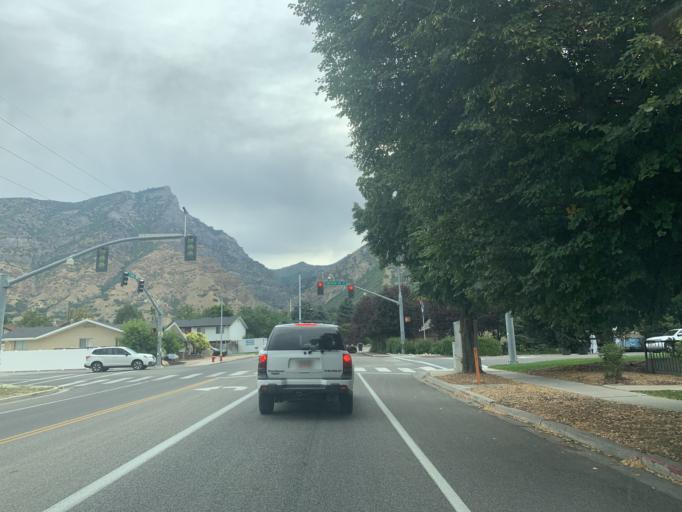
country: US
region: Utah
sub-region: Utah County
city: Provo
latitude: 40.2631
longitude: -111.6478
